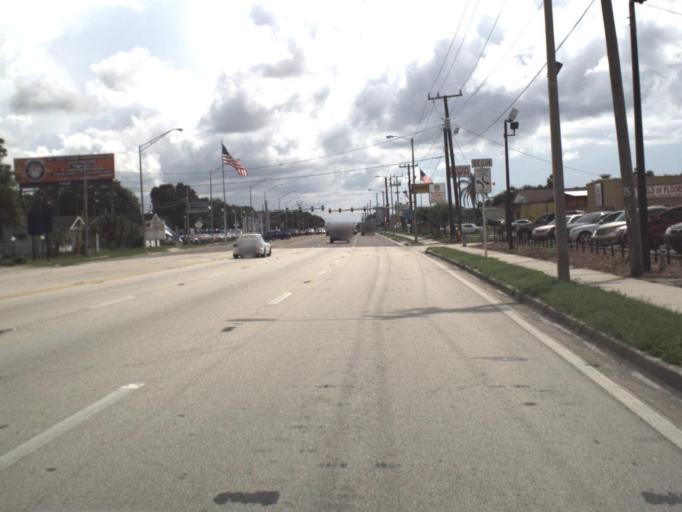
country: US
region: Florida
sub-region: Manatee County
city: West Samoset
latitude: 27.4795
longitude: -82.5631
